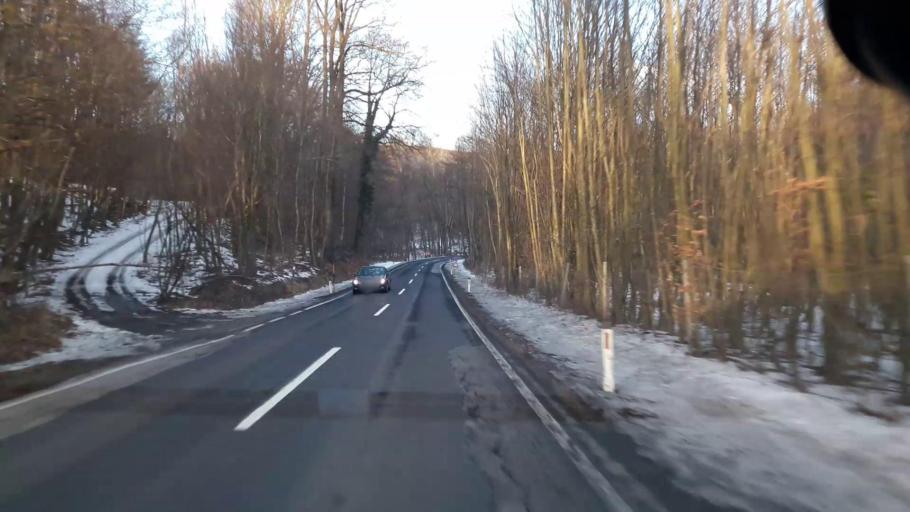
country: AT
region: Lower Austria
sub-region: Politischer Bezirk Wien-Umgebung
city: Mauerbach
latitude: 48.2669
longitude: 16.1708
